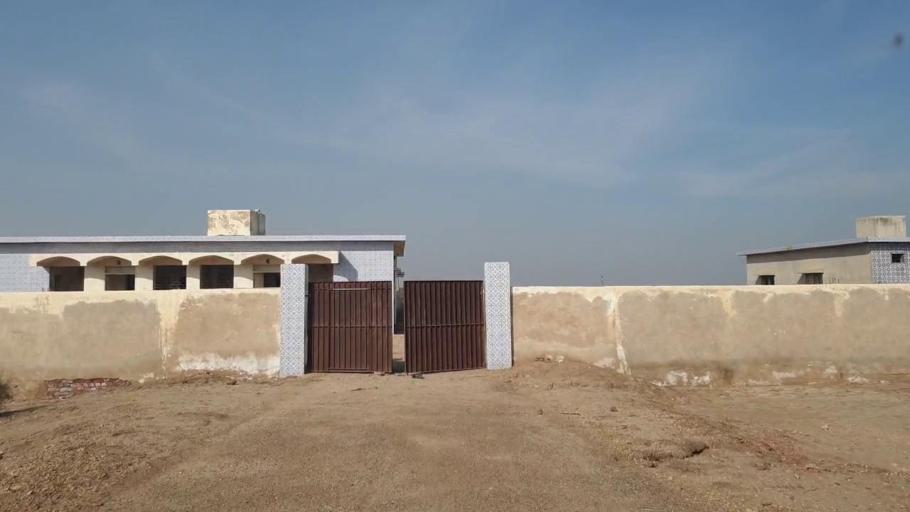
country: PK
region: Sindh
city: Sann
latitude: 25.9140
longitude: 68.2303
